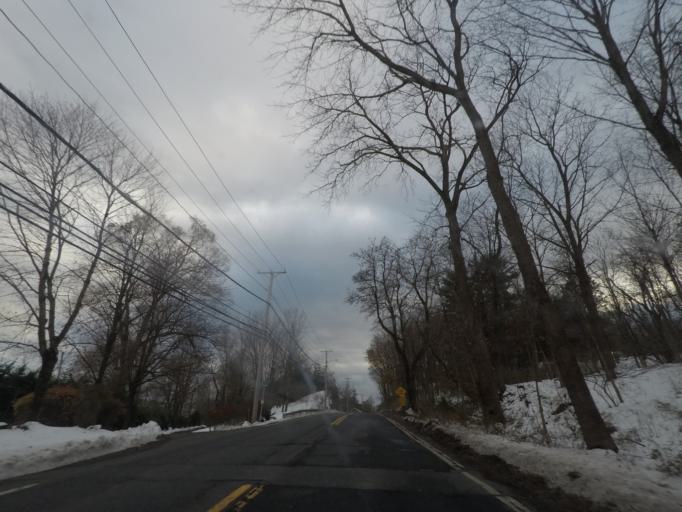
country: US
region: New York
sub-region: Ulster County
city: Kingston
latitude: 41.9157
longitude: -74.0154
